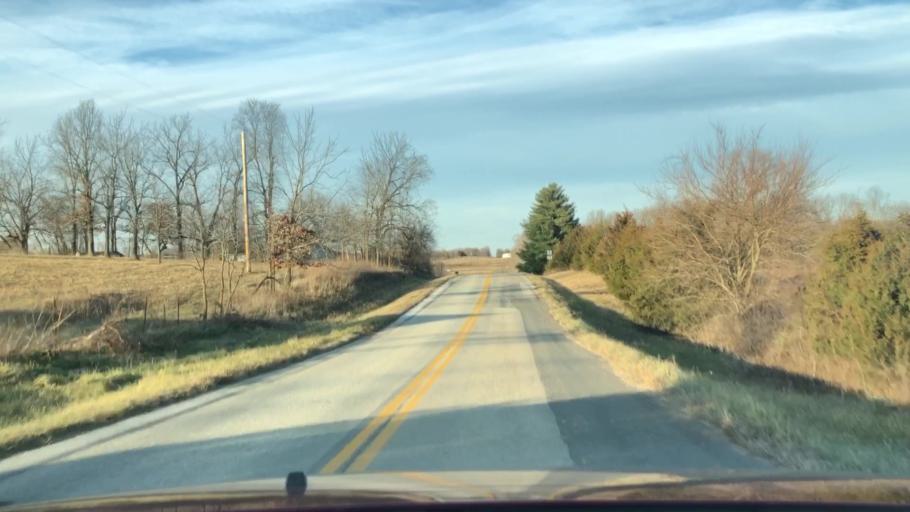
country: US
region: Missouri
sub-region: Wright County
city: Mansfield
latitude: 37.1093
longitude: -92.6295
